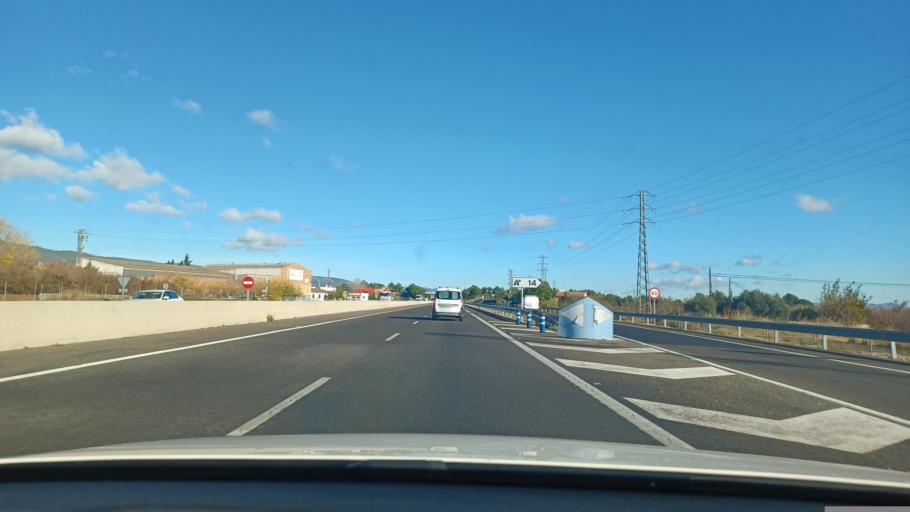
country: ES
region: Catalonia
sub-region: Provincia de Tarragona
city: La Selva
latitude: 41.2009
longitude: 1.1445
